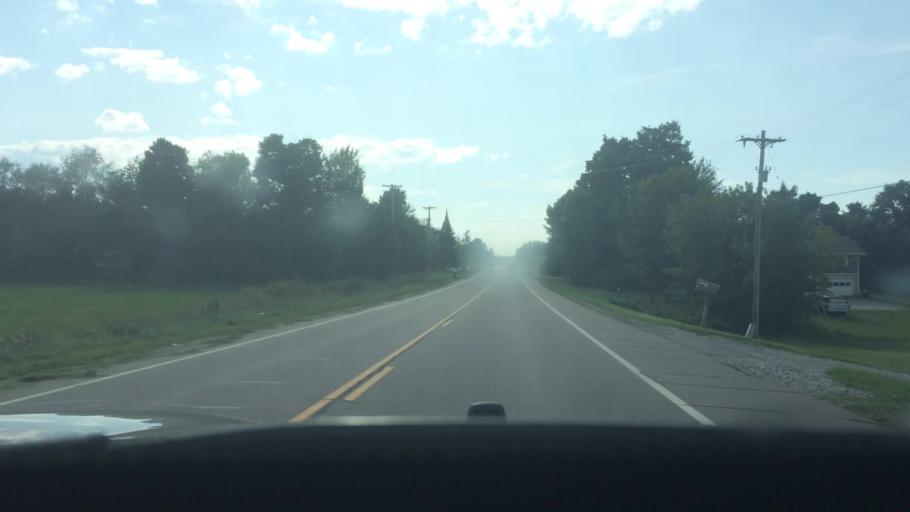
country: US
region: New York
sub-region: Franklin County
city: Malone
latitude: 44.8458
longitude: -74.1696
